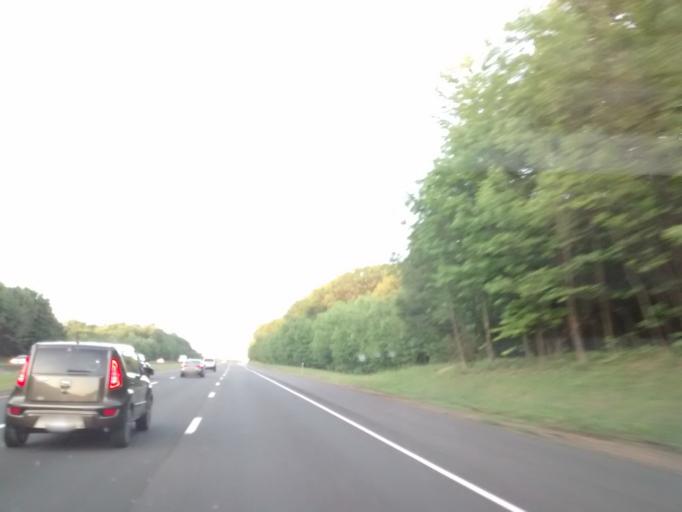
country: US
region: Connecticut
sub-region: Tolland County
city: Stafford Springs
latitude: 41.9350
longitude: -72.2364
